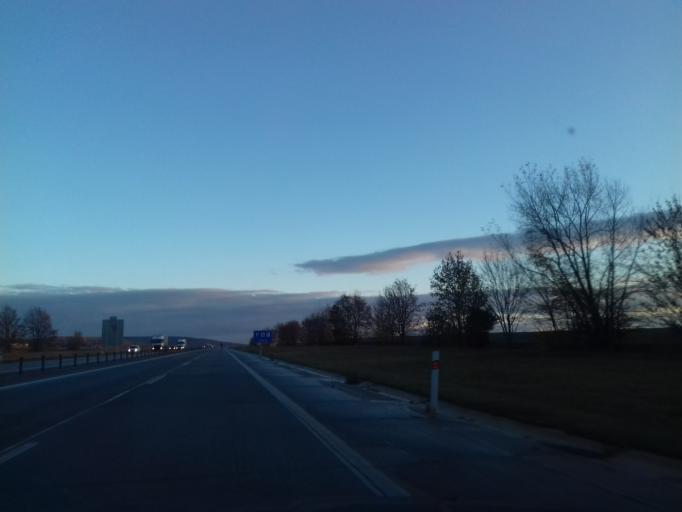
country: CZ
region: South Moravian
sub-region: Okres Vyskov
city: Vyskov
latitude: 49.2885
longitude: 17.0206
